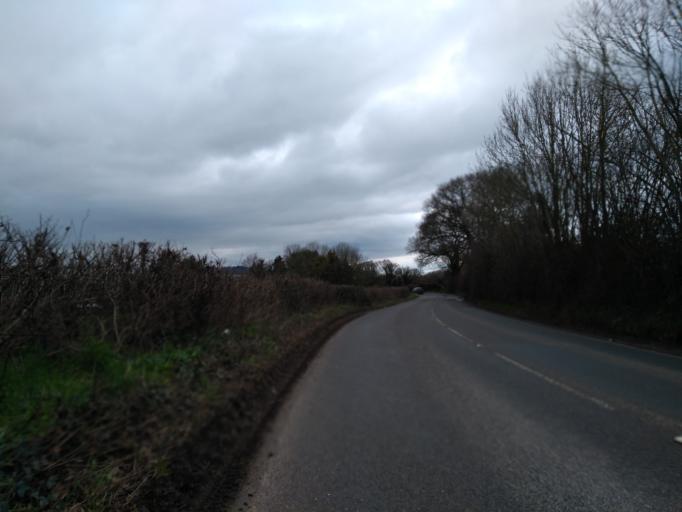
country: GB
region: England
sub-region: Devon
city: Heavitree
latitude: 50.7969
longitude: -3.4969
